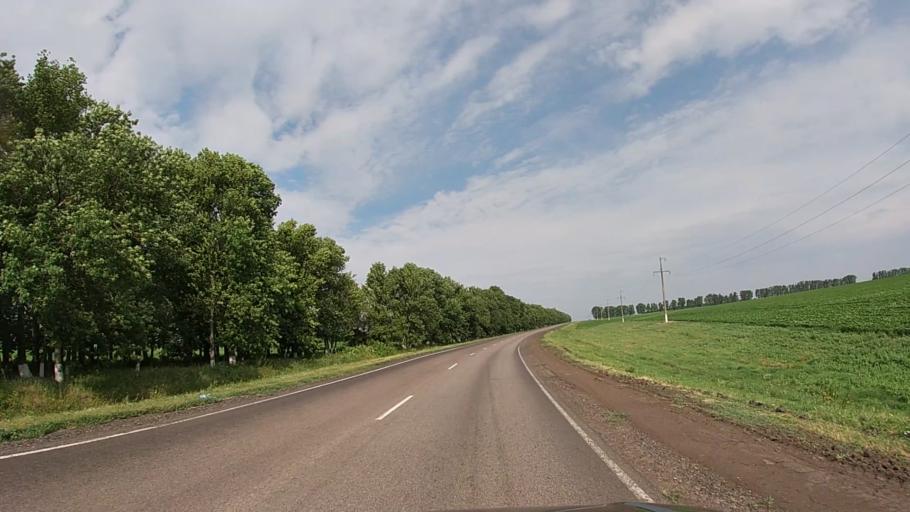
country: RU
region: Belgorod
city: Krasnaya Yaruga
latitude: 50.8020
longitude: 35.5569
